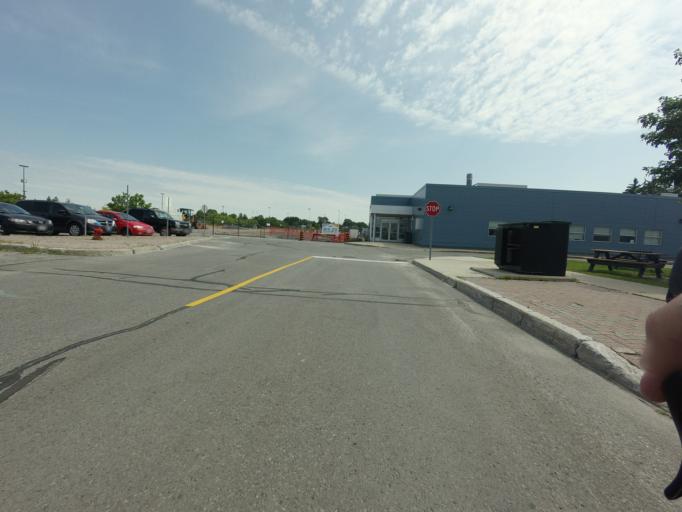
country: CA
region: Ontario
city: Ottawa
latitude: 45.3501
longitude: -75.7533
